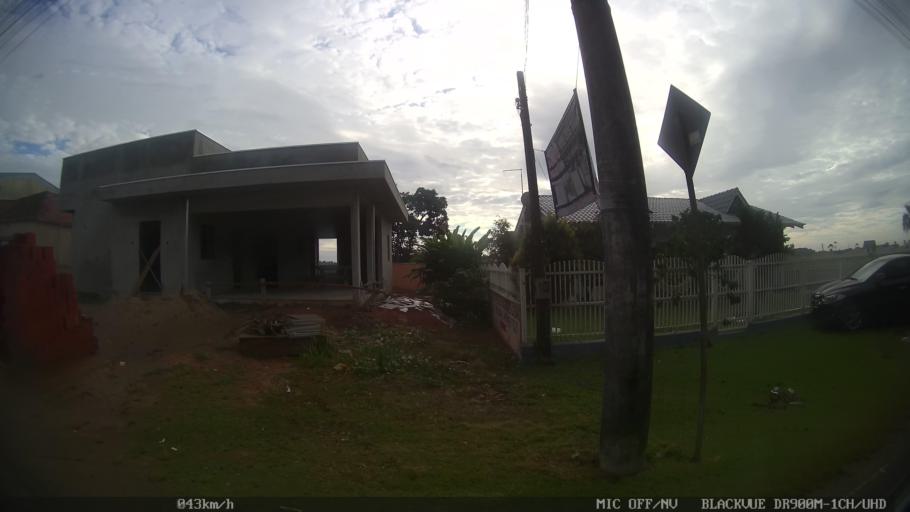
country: BR
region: Santa Catarina
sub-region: Barra Velha
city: Barra Velha
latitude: -26.6237
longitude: -48.7043
